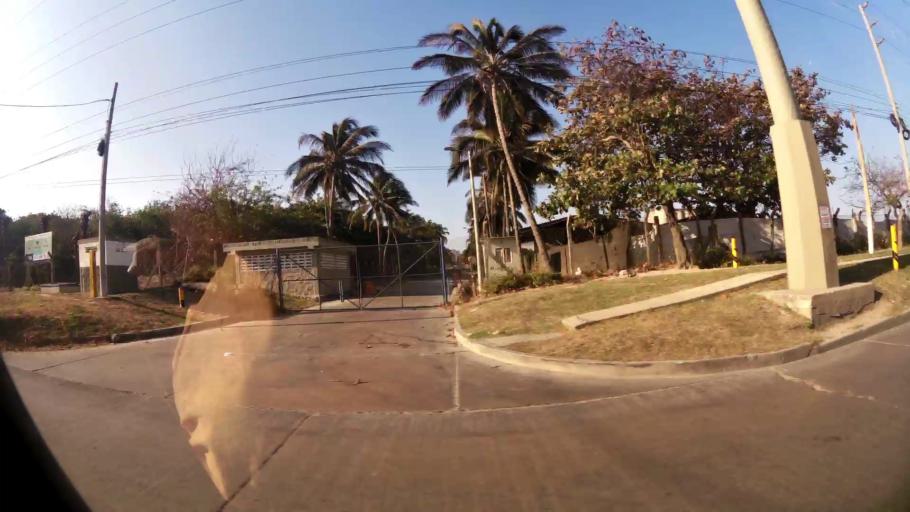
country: CO
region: Atlantico
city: Barranquilla
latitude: 11.0345
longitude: -74.8131
